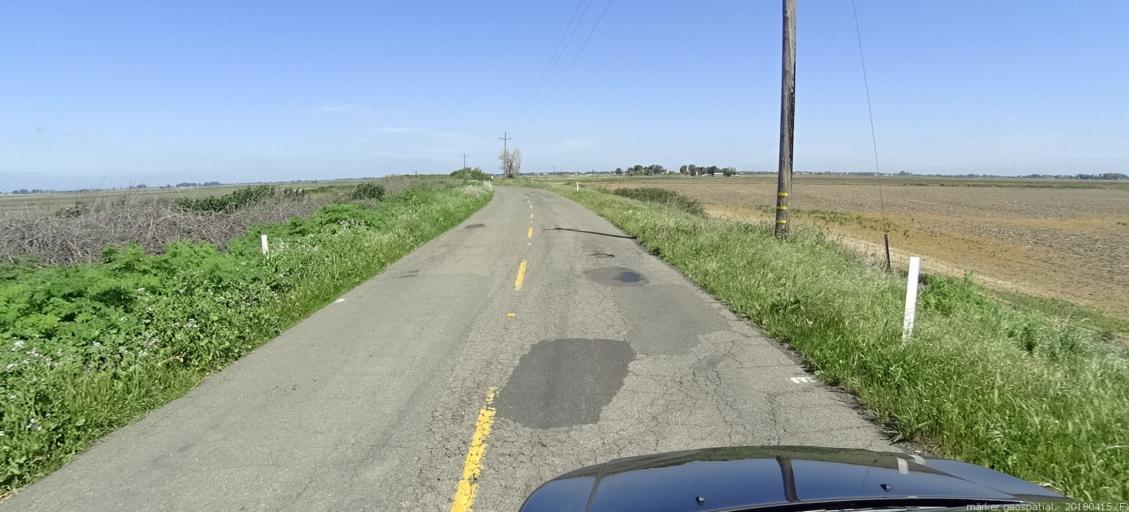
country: US
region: California
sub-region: Solano County
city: Rio Vista
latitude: 38.1244
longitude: -121.6247
